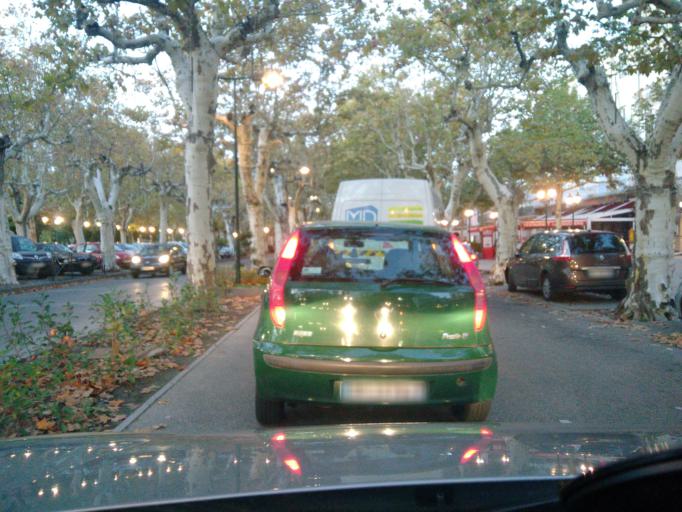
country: FR
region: Rhone-Alpes
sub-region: Departement de la Drome
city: Montelimar
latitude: 44.5593
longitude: 4.7480
